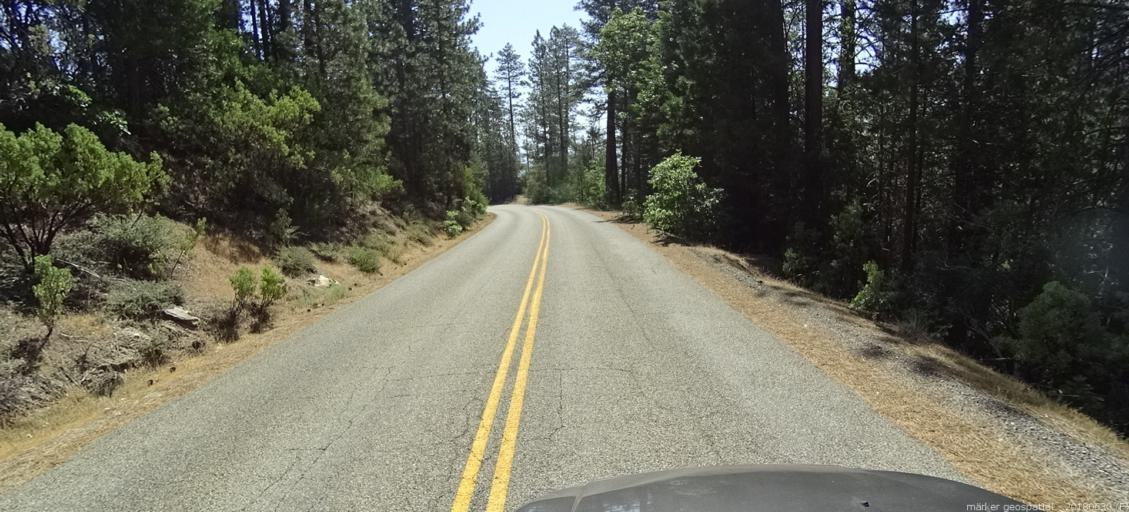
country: US
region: California
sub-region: Madera County
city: Oakhurst
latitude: 37.3671
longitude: -119.3925
